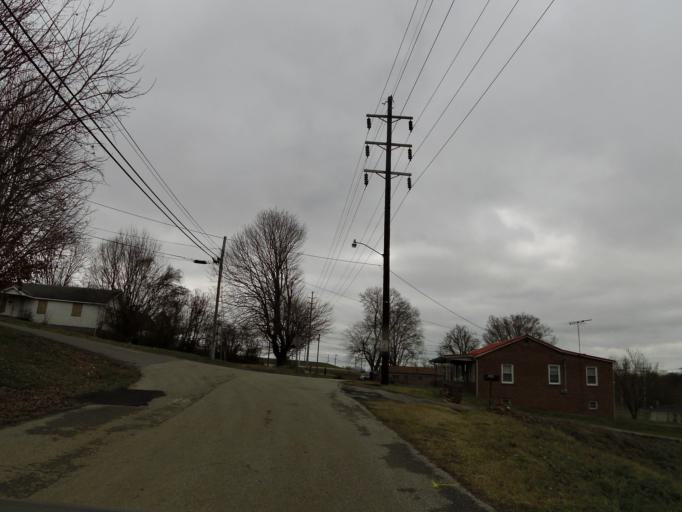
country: US
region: Tennessee
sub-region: Jefferson County
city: Jefferson City
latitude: 36.1298
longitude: -83.4919
